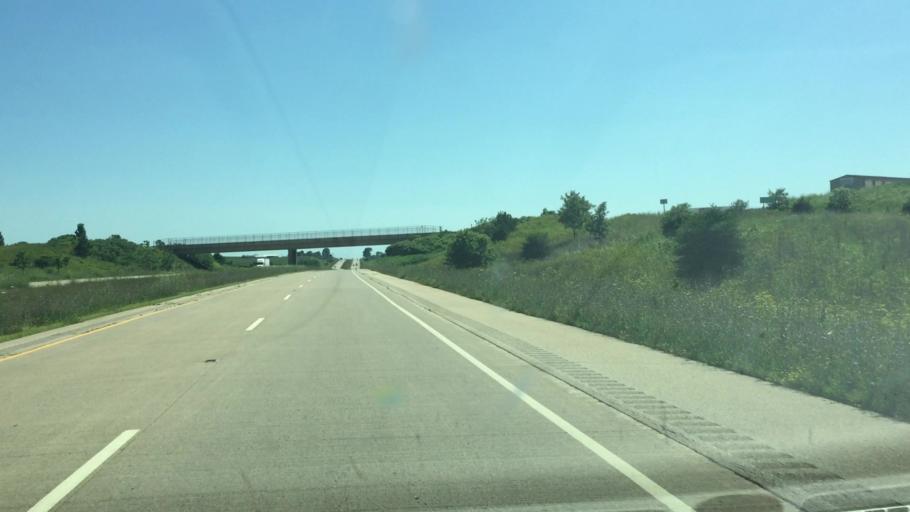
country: US
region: Wisconsin
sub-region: Grant County
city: Dickeyville
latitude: 42.6190
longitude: -90.5852
